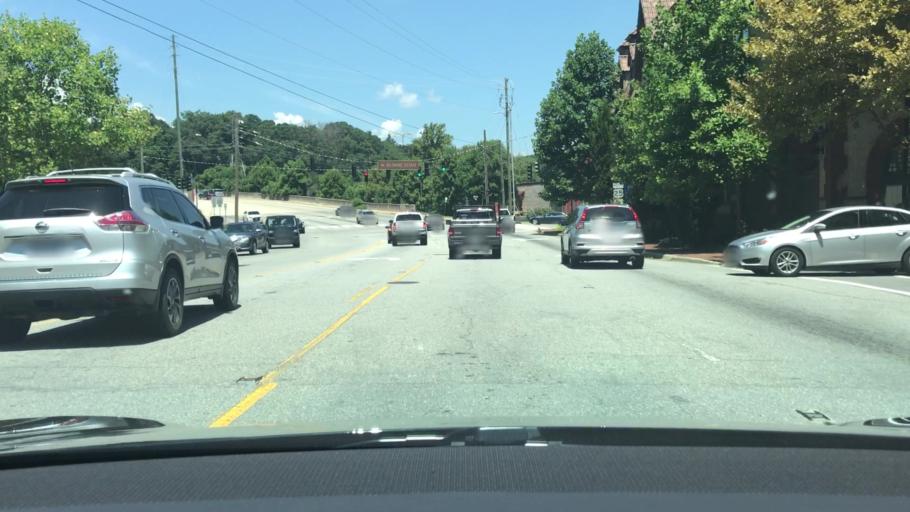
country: US
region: North Carolina
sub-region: Buncombe County
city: Asheville
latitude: 35.5663
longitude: -82.5442
